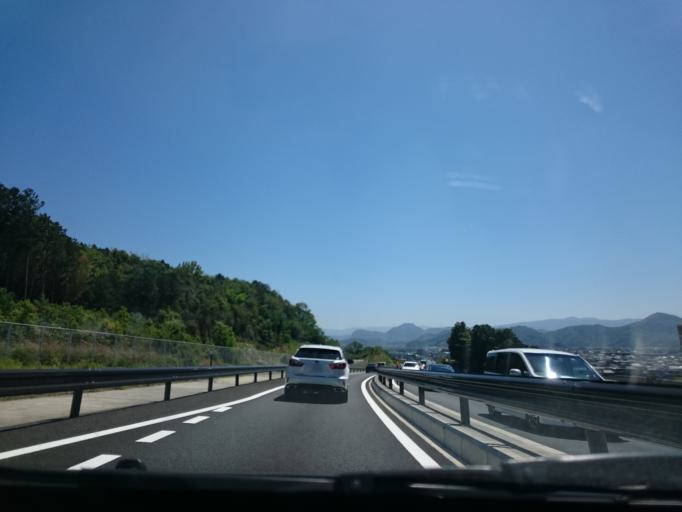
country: JP
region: Shizuoka
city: Mishima
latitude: 35.1025
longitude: 138.9486
